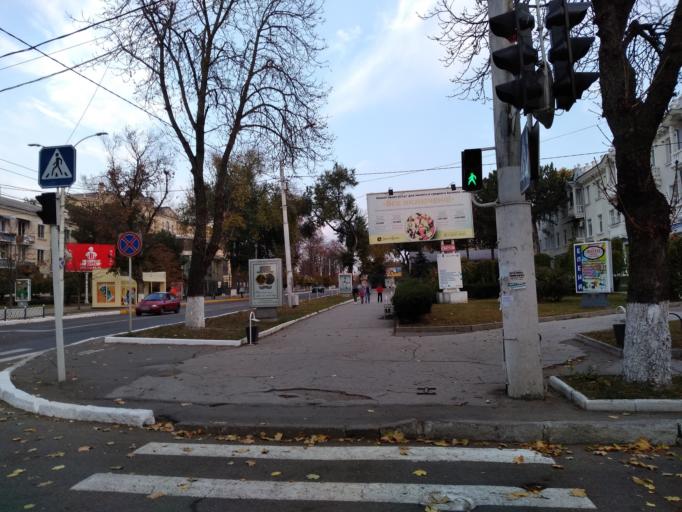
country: MD
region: Telenesti
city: Tiraspolul Nou
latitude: 46.8365
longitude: 29.6248
